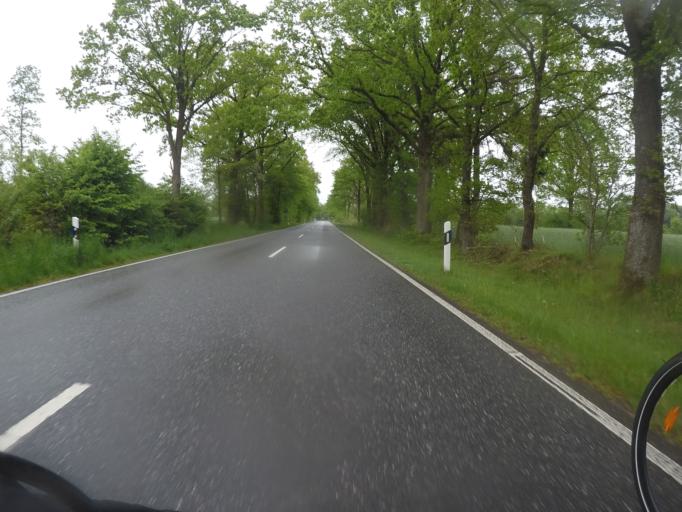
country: DE
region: Schleswig-Holstein
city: Heidmuhlen
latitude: 53.9519
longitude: 10.0851
